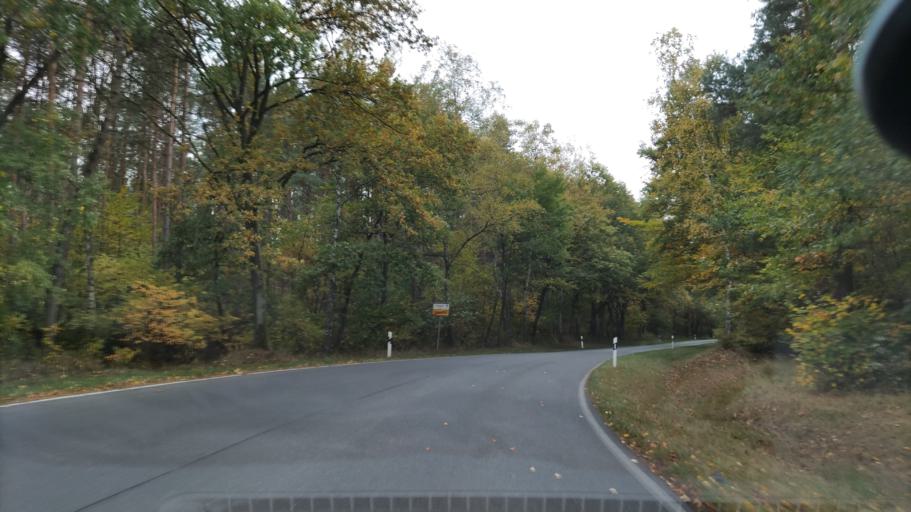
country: DE
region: Mecklenburg-Vorpommern
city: Boizenburg
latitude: 53.3782
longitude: 10.8537
